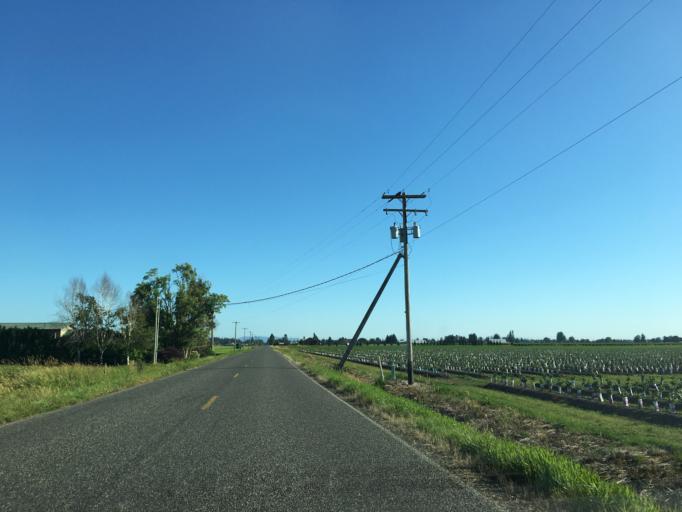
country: US
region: Washington
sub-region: Whatcom County
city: Lynden
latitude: 48.9760
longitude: -122.4519
